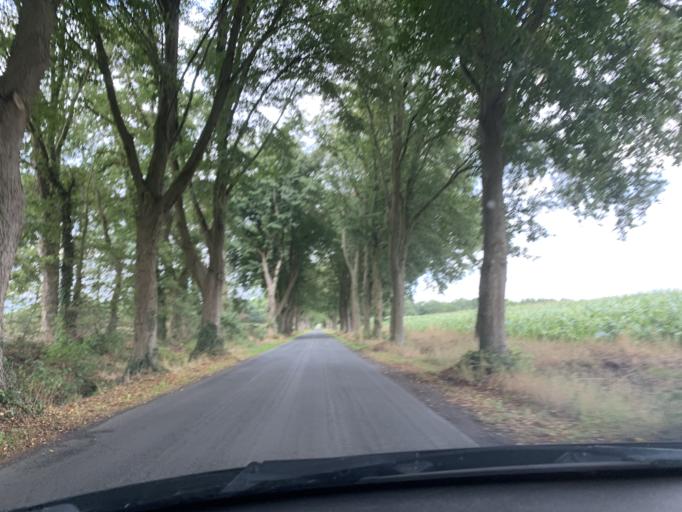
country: DE
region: Lower Saxony
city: Apen
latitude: 53.2524
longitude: 7.8580
